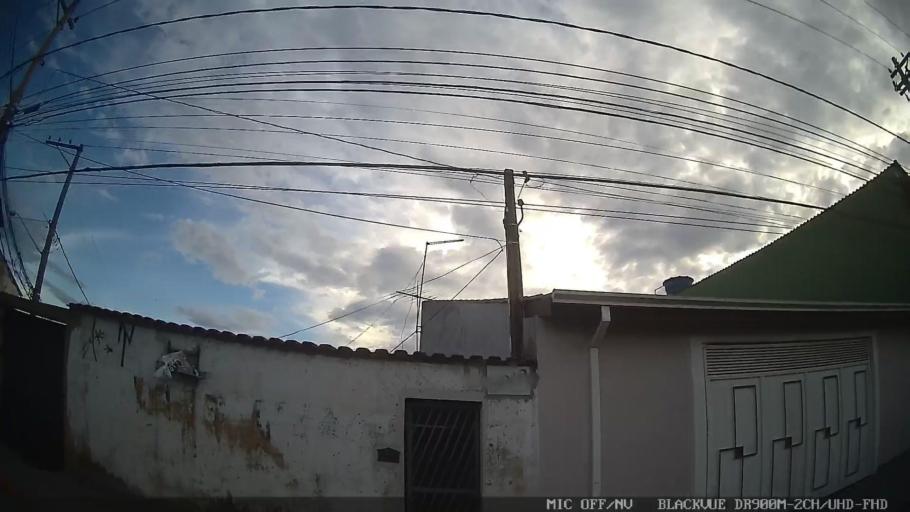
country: BR
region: Sao Paulo
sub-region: Mogi das Cruzes
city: Mogi das Cruzes
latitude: -23.5331
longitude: -46.1753
